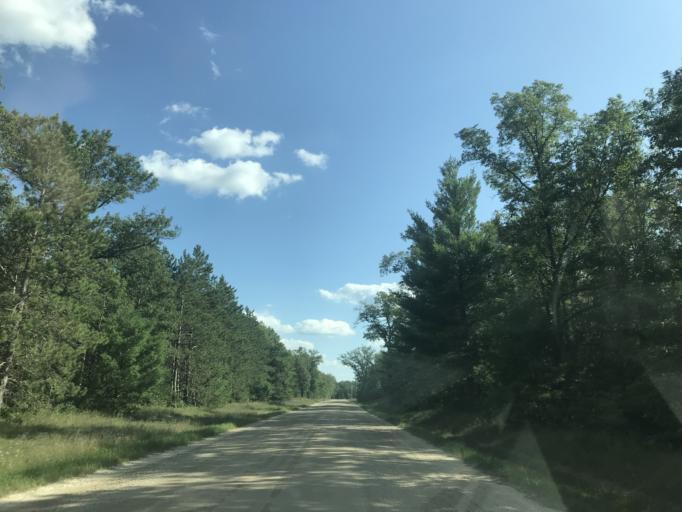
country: US
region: Michigan
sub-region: Newaygo County
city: Newaygo
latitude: 43.4415
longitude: -85.7326
